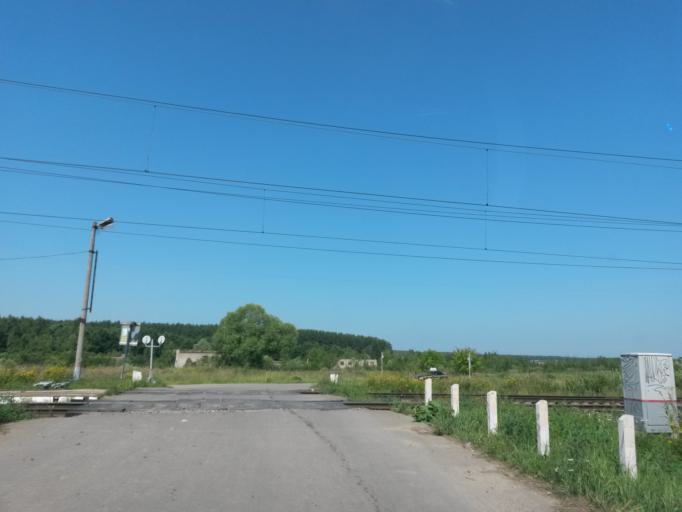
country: RU
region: Moskovskaya
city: Stolbovaya
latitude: 55.2581
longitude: 37.4825
